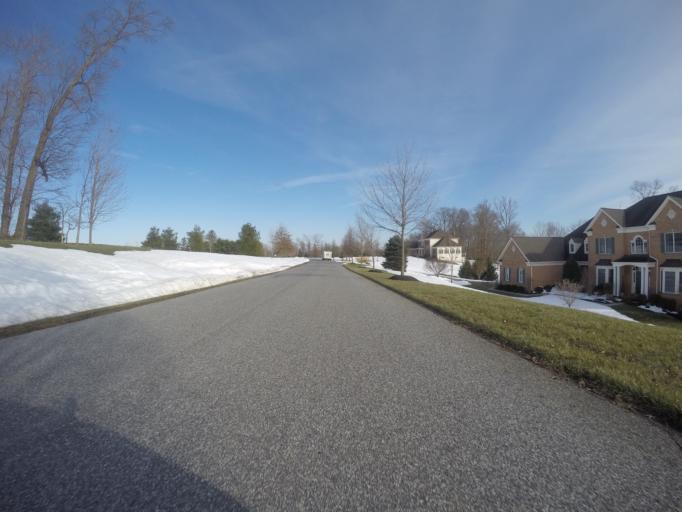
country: US
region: Maryland
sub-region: Baltimore County
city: Hunt Valley
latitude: 39.5654
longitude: -76.6590
